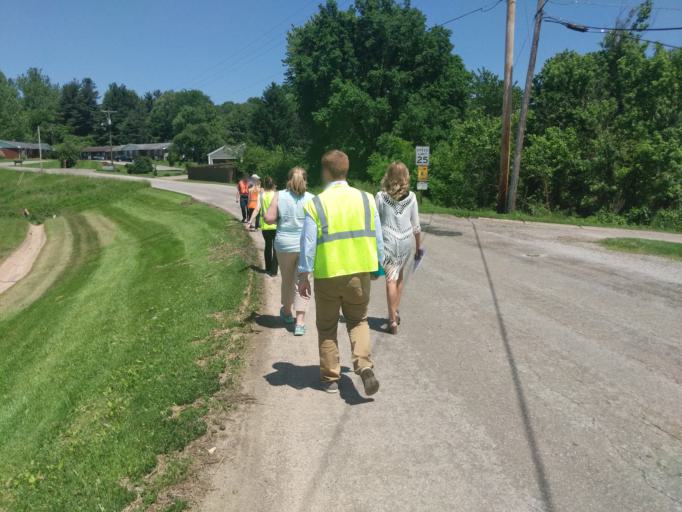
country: US
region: Ohio
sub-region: Washington County
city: Reno
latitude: 39.3938
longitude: -81.4007
